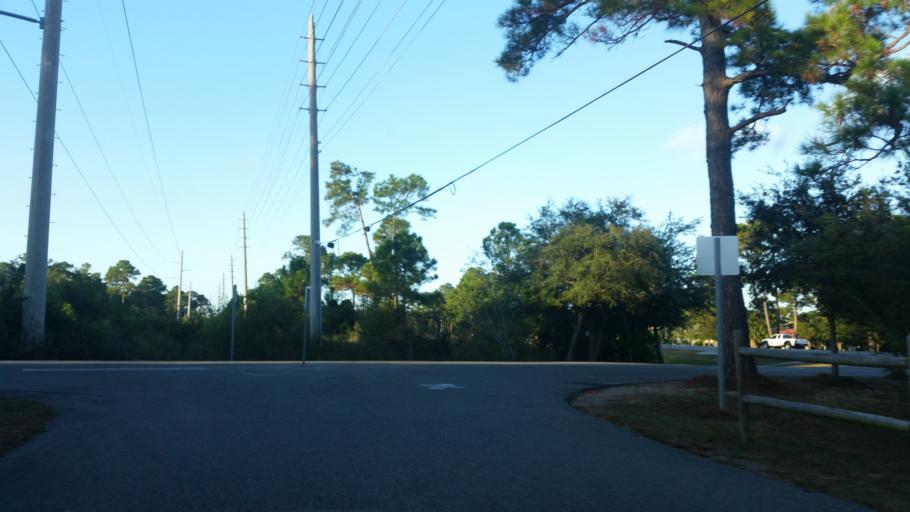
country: US
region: Alabama
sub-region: Baldwin County
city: Orange Beach
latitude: 30.2804
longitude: -87.5814
